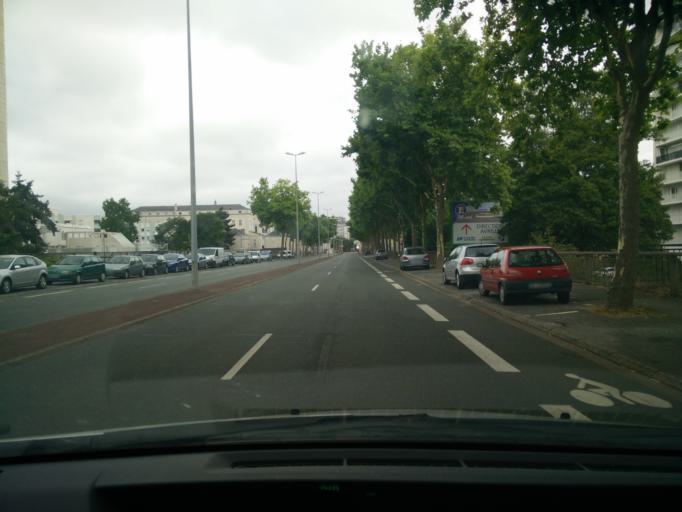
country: FR
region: Pays de la Loire
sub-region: Departement de Maine-et-Loire
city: Angers
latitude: 47.4704
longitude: -0.5354
